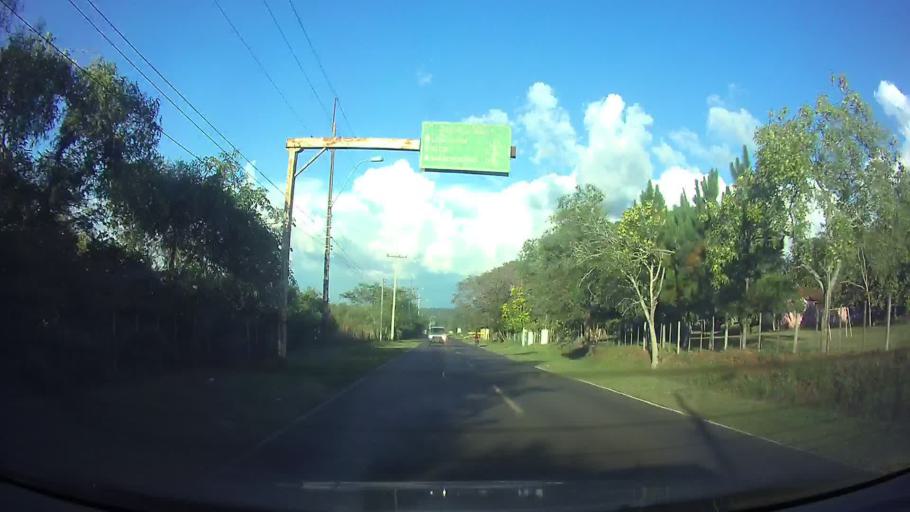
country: PY
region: Cordillera
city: Emboscada
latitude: -25.1932
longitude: -57.3138
